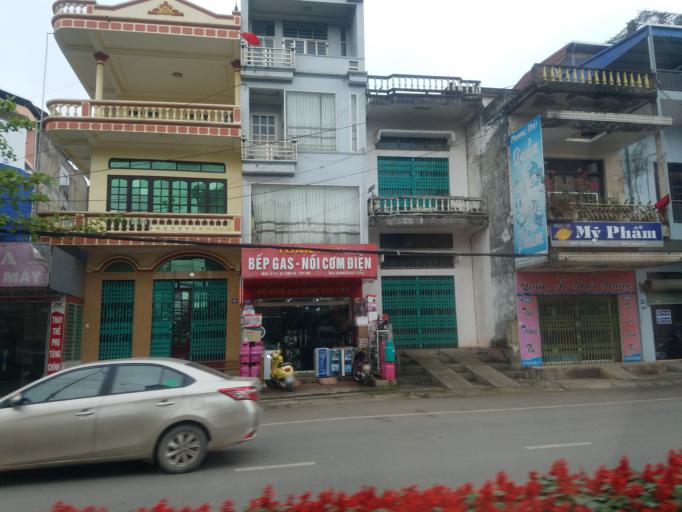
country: VN
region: Thai Nguyen
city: Thanh Pho Thai Nguyen
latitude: 21.5917
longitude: 105.8440
